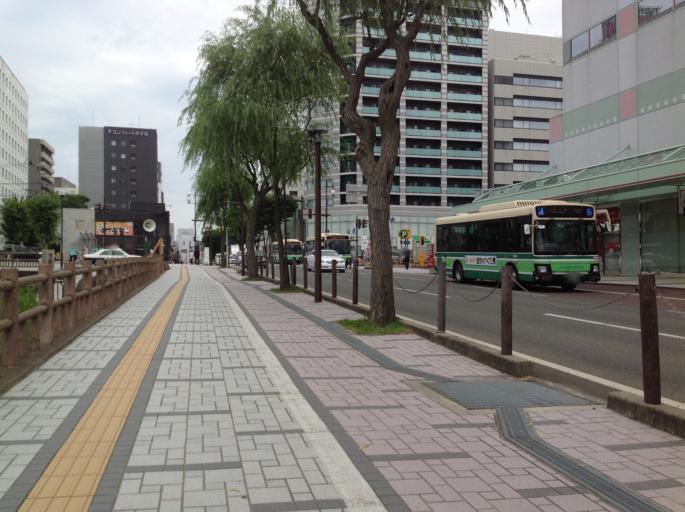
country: JP
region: Akita
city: Akita
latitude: 39.7180
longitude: 140.1244
